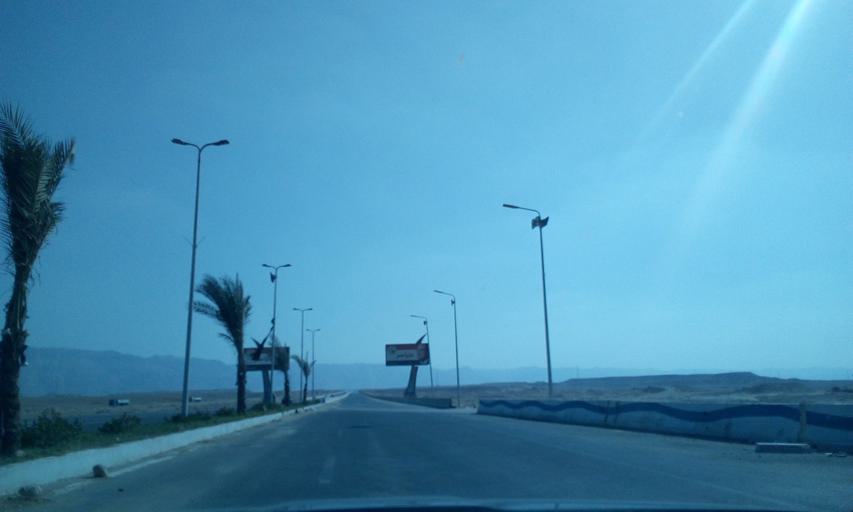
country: EG
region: As Suways
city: Ain Sukhna
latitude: 29.6415
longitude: 32.2275
